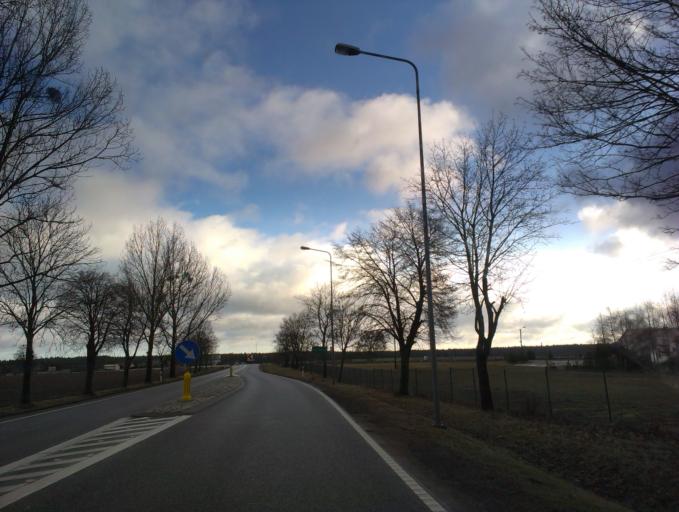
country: PL
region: Pomeranian Voivodeship
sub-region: Powiat czluchowski
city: Czluchow
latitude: 53.6352
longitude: 17.2820
